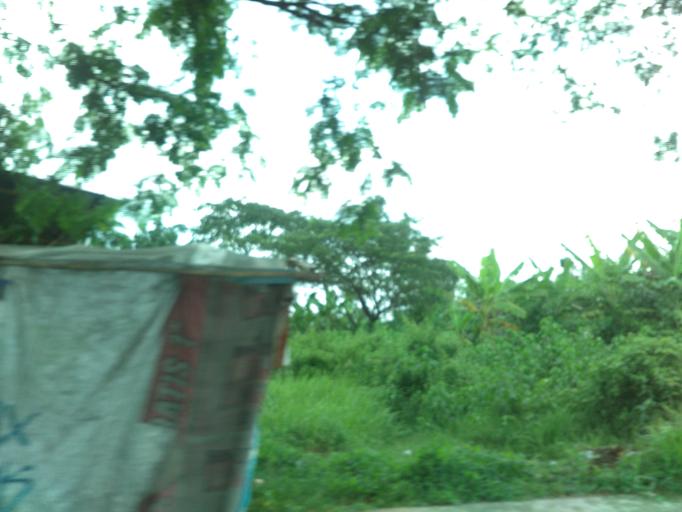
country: ID
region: Central Java
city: Ceper
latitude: -7.6559
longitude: 110.6790
